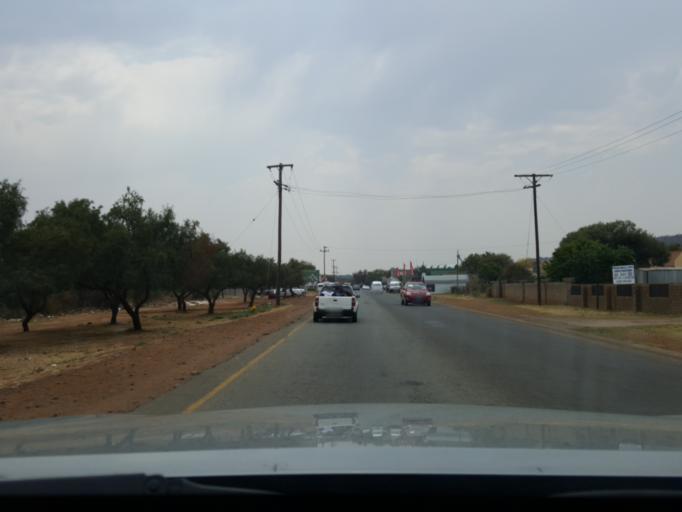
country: ZA
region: North-West
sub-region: Ngaka Modiri Molema District Municipality
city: Zeerust
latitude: -25.4959
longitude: 25.9841
